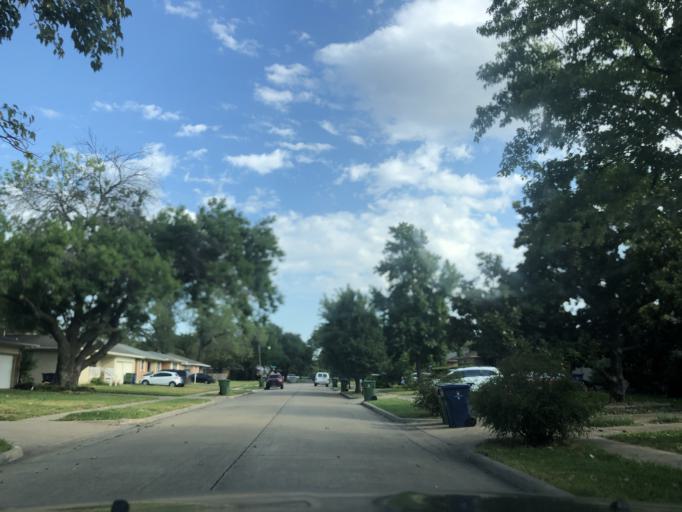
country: US
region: Texas
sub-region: Dallas County
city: Garland
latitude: 32.8874
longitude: -96.6591
